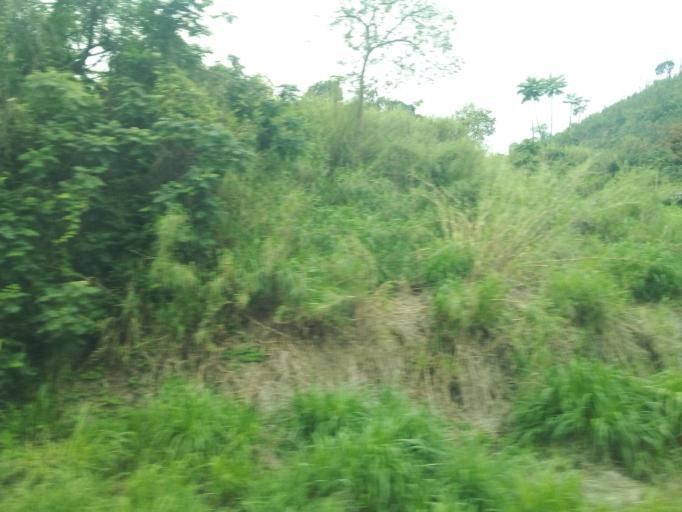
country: BR
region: Minas Gerais
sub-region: Joao Monlevade
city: Joao Monlevade
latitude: -19.8262
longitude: -43.1262
